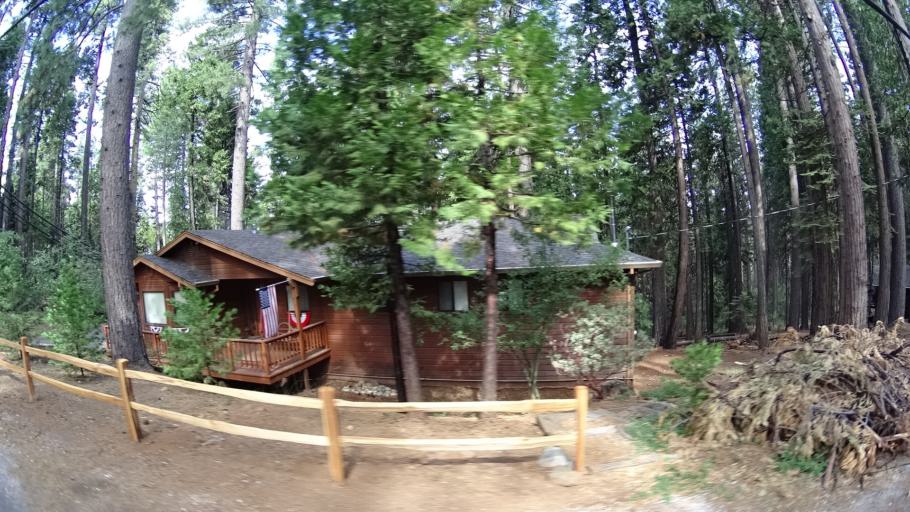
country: US
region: California
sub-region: Calaveras County
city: Arnold
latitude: 38.2617
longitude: -120.3348
